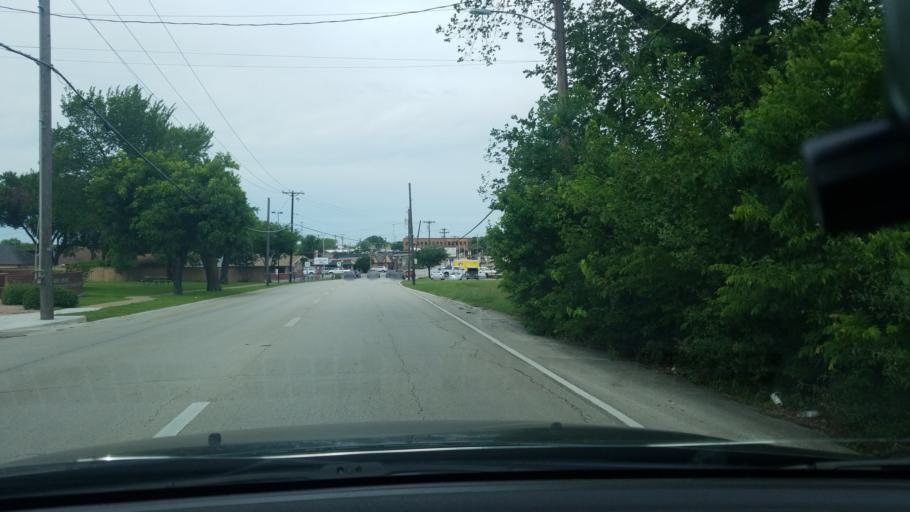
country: US
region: Texas
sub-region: Dallas County
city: Mesquite
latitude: 32.7668
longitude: -96.5954
